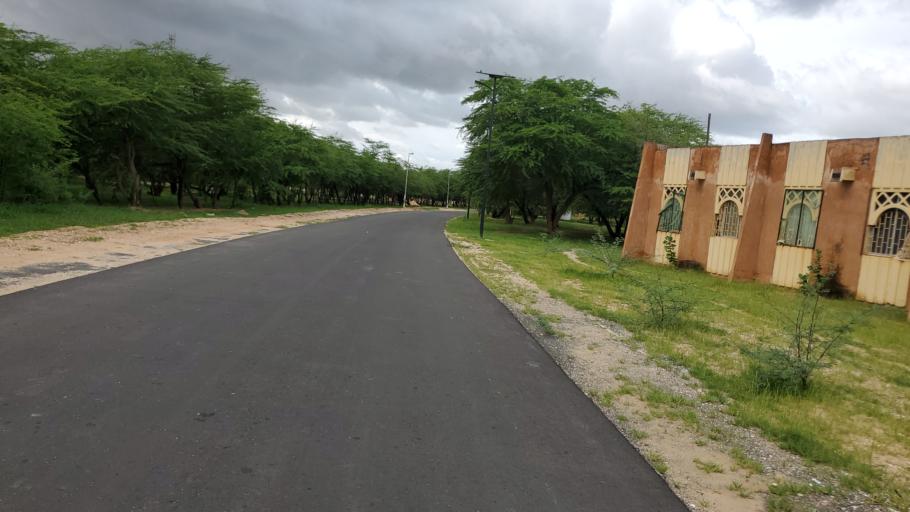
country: SN
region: Saint-Louis
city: Saint-Louis
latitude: 16.0624
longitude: -16.4285
